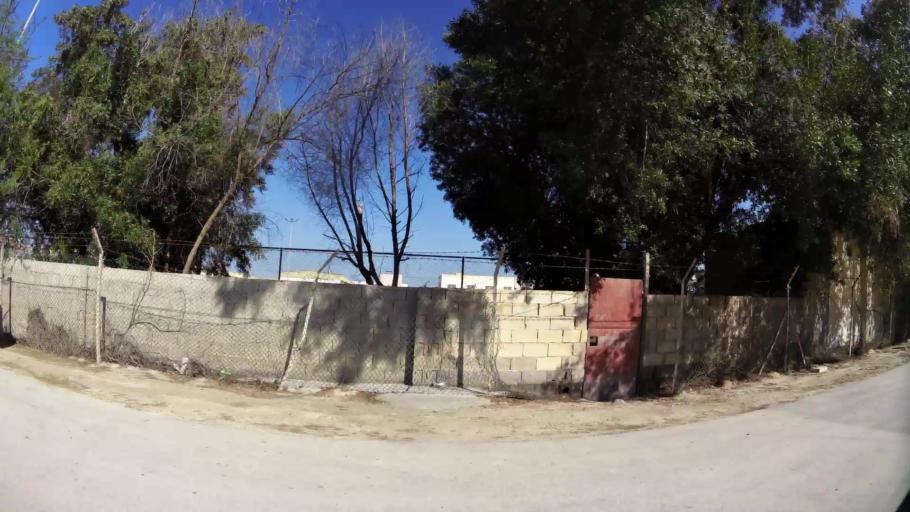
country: BH
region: Manama
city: Manama
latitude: 26.2078
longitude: 50.5714
